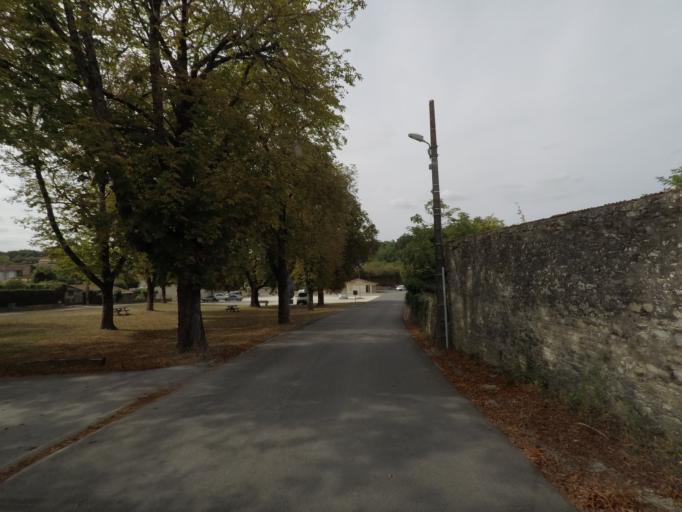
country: FR
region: Poitou-Charentes
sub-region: Departement de la Charente
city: Champagne-Mouton
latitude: 45.9900
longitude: 0.4103
